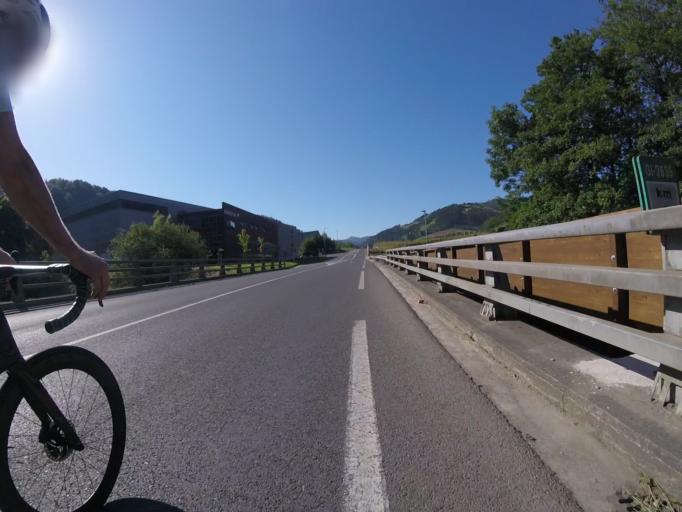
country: ES
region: Basque Country
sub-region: Provincia de Guipuzcoa
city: Azpeitia
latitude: 43.1635
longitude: -2.2466
